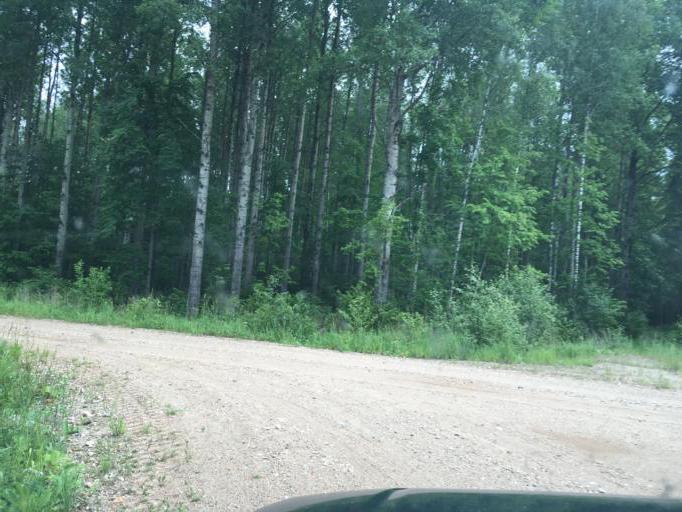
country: LV
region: Vilaka
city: Vilaka
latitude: 57.3824
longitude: 27.5479
